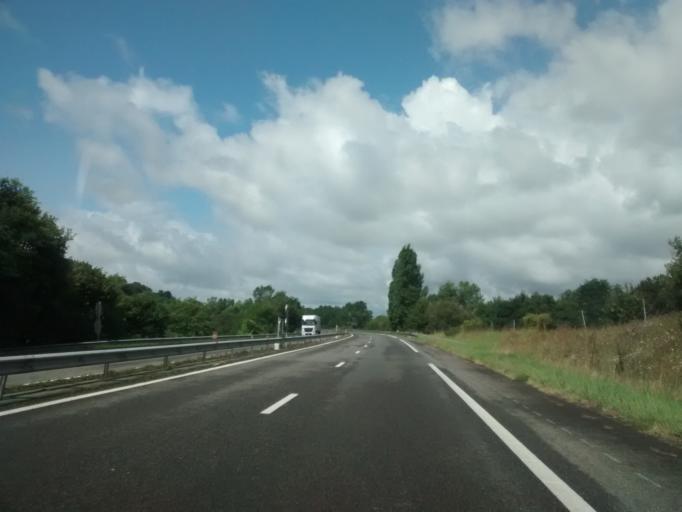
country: FR
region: Aquitaine
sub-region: Departement des Pyrenees-Atlantiques
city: Puyoo
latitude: 43.5101
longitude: -0.8825
